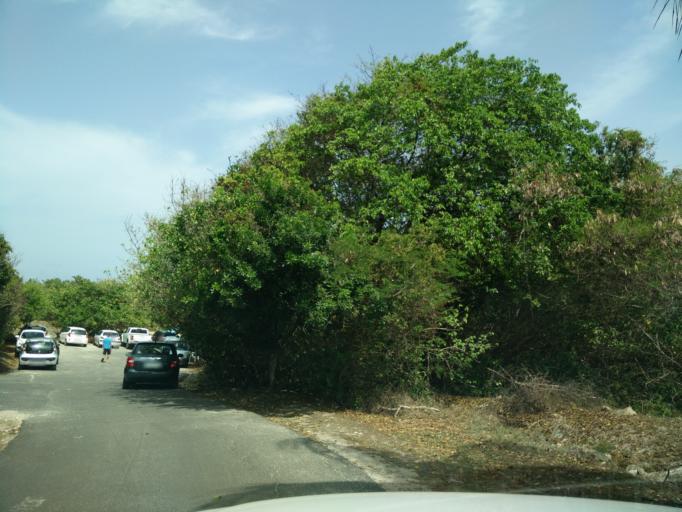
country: GP
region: Guadeloupe
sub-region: Guadeloupe
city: Sainte-Anne
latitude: 16.2422
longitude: -61.3400
